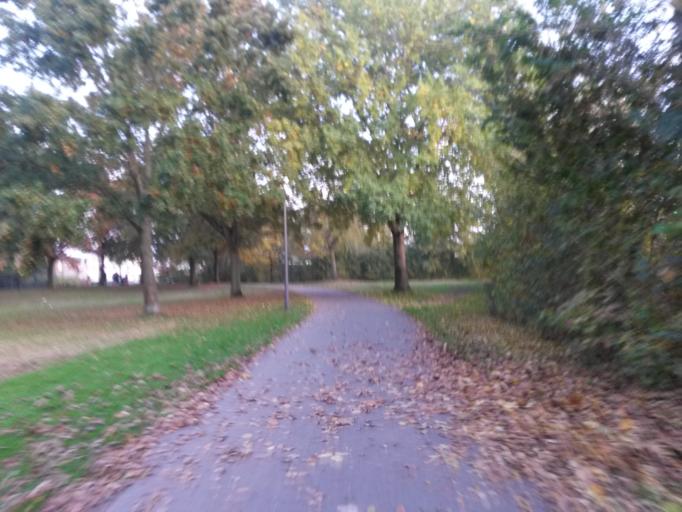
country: DE
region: Bremen
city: Bremen
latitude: 53.0466
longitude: 8.8389
